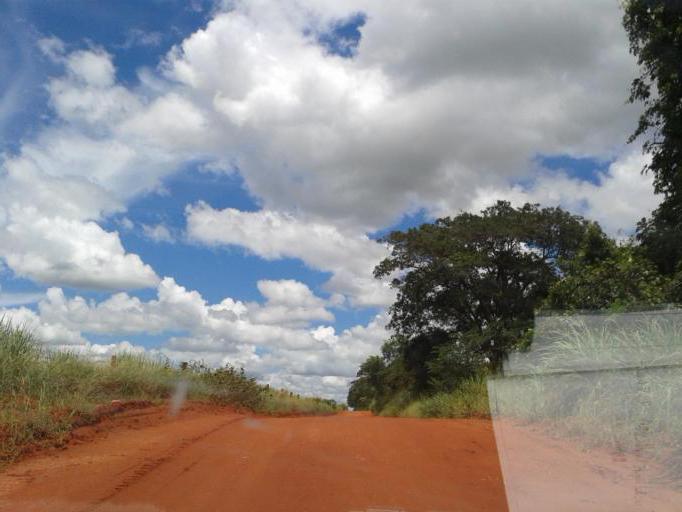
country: BR
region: Minas Gerais
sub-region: Santa Vitoria
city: Santa Vitoria
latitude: -18.8326
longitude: -50.0786
